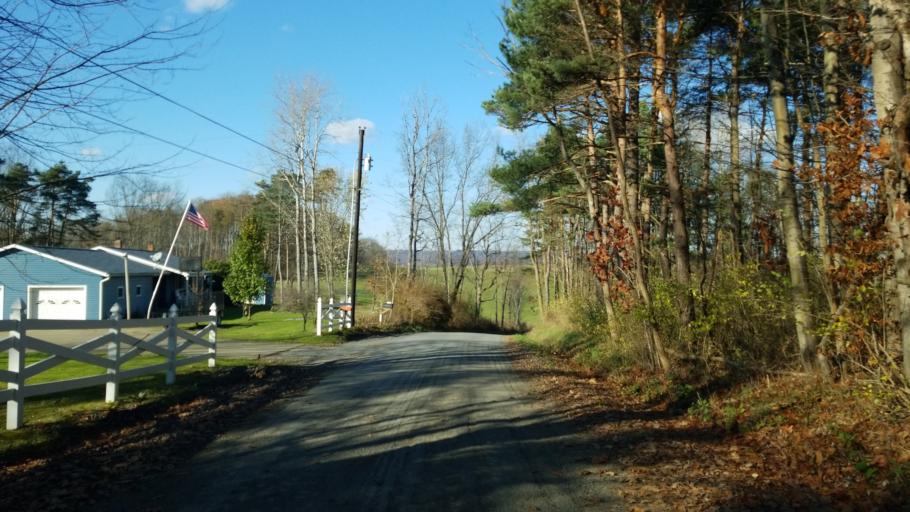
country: US
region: Pennsylvania
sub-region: Clearfield County
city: Treasure Lake
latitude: 41.1546
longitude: -78.6607
